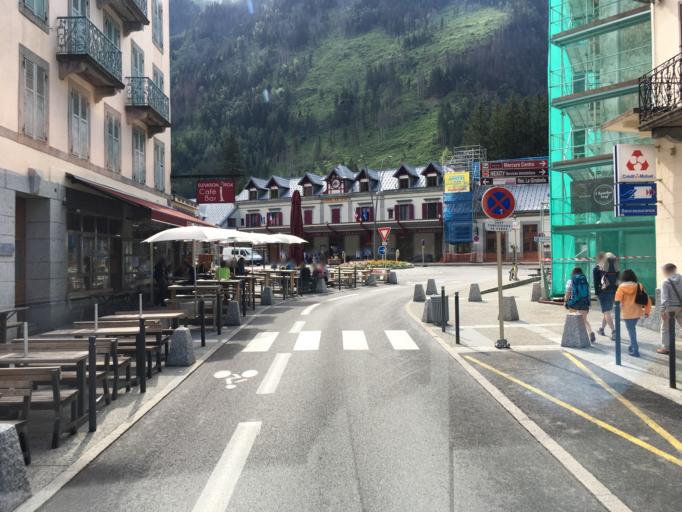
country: FR
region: Rhone-Alpes
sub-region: Departement de la Haute-Savoie
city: Chamonix-Mont-Blanc
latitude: 45.9230
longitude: 6.8729
